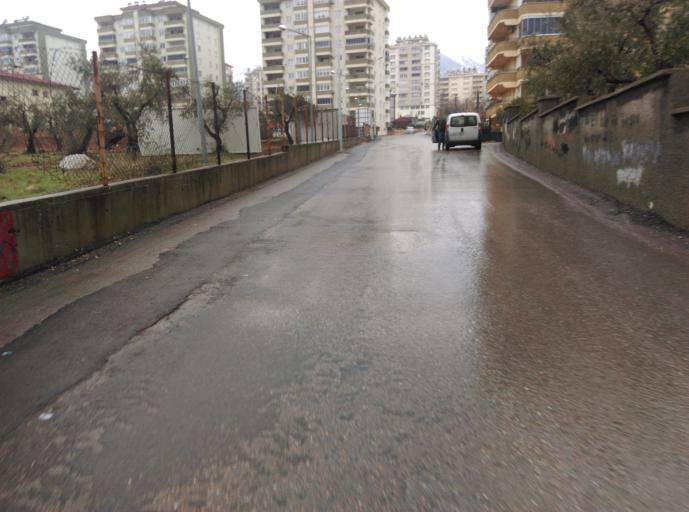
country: TR
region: Kahramanmaras
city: Kahramanmaras
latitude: 37.5845
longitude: 36.8916
